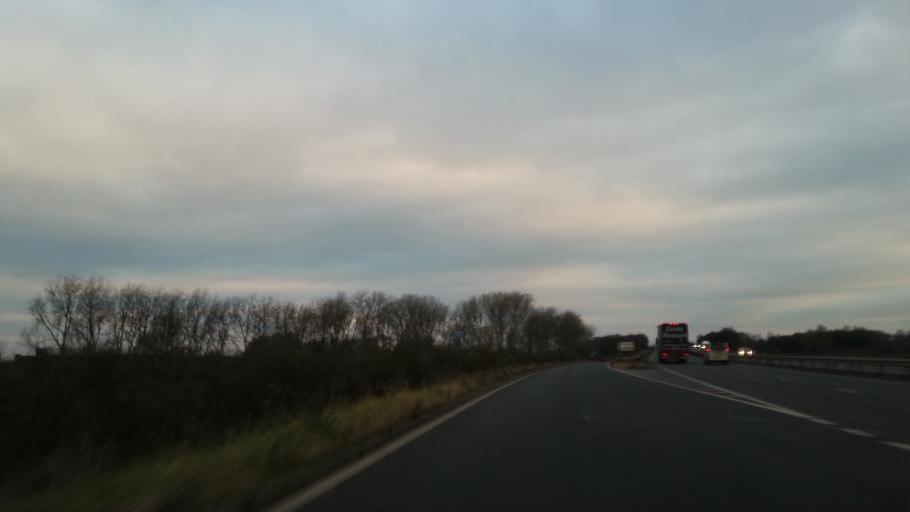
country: GB
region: England
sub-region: Nottinghamshire
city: Newark on Trent
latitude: 53.1162
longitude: -0.8164
